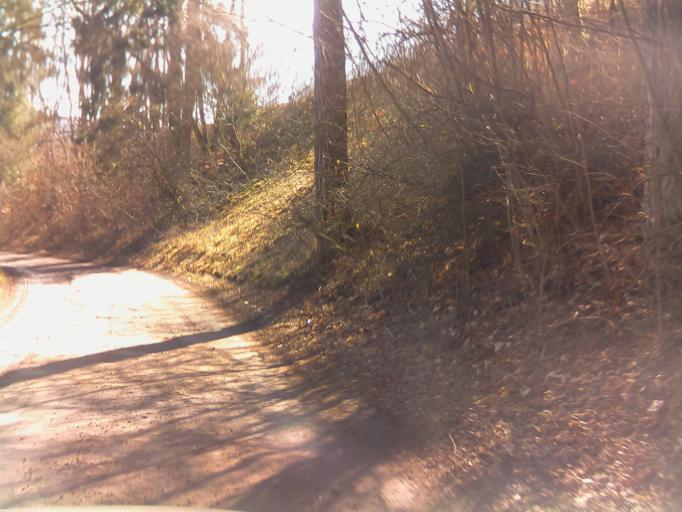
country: DE
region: Thuringia
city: Belrieth
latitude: 50.5416
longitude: 10.4993
